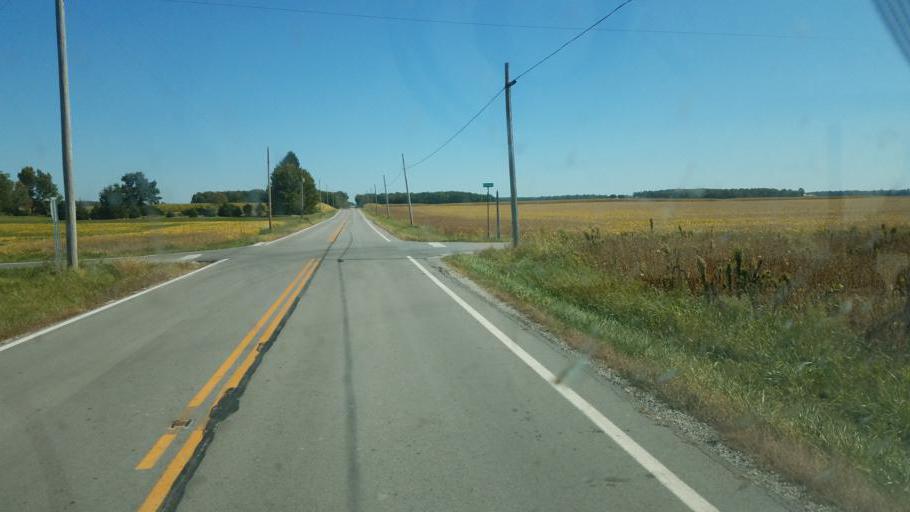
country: US
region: Ohio
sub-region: Crawford County
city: Bucyrus
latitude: 40.9503
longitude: -82.9978
